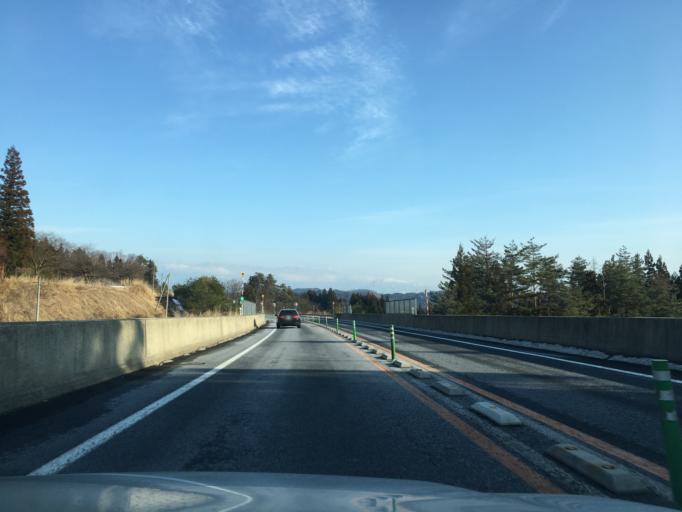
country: JP
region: Yamagata
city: Sagae
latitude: 38.4299
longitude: 140.1485
